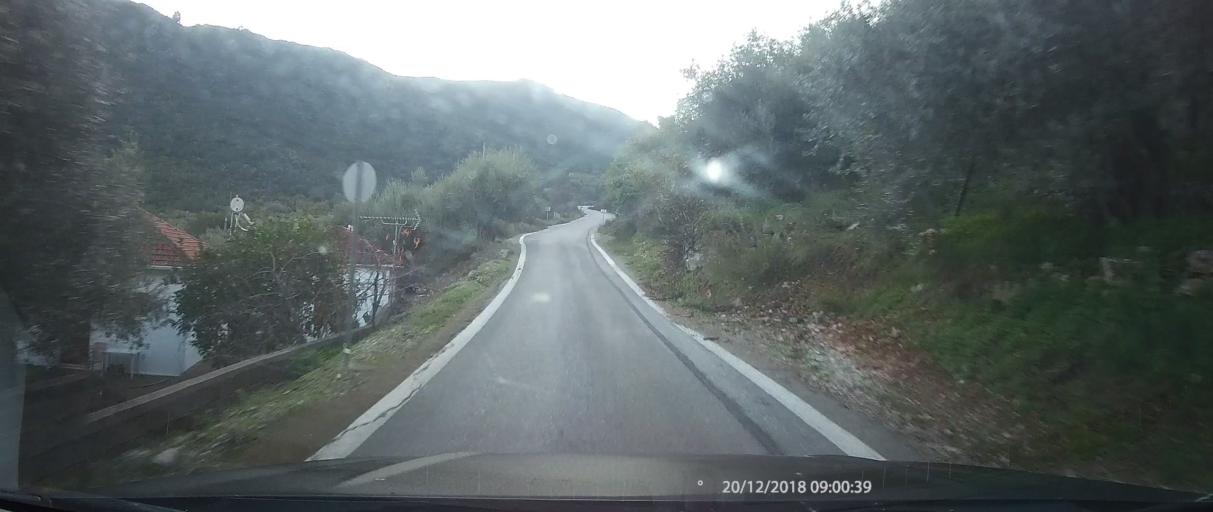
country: GR
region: Peloponnese
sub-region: Nomos Lakonias
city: Sykea
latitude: 36.9590
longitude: 22.9894
